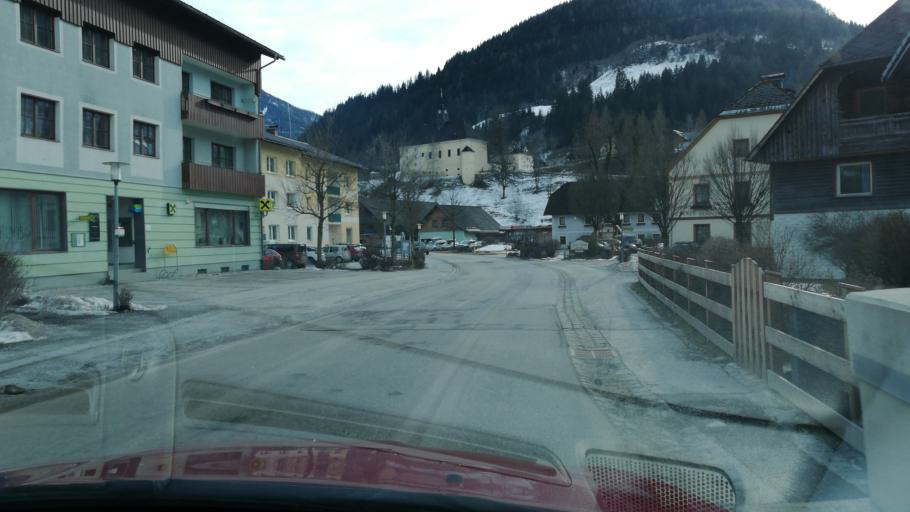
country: AT
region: Styria
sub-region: Politischer Bezirk Liezen
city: Donnersbach
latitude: 47.4667
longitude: 14.1280
